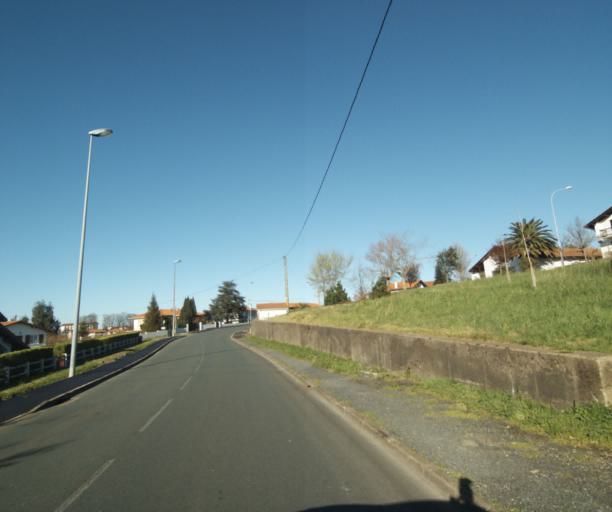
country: FR
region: Aquitaine
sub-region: Departement des Pyrenees-Atlantiques
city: Hendaye
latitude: 43.3644
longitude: -1.7609
